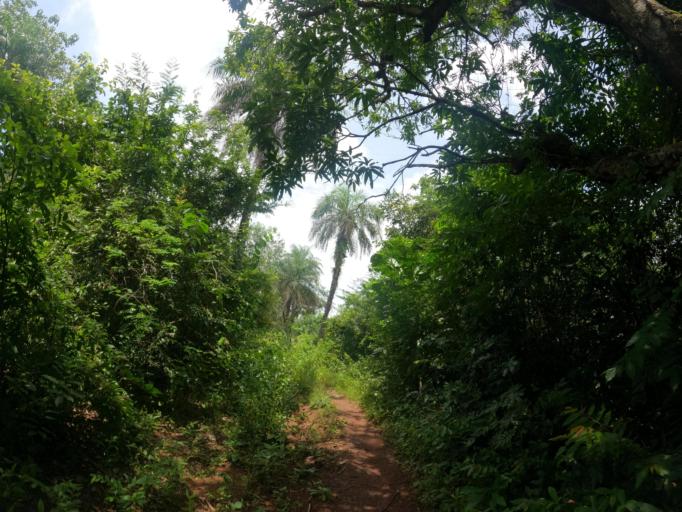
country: SL
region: Northern Province
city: Binkolo
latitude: 9.1476
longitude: -12.2463
